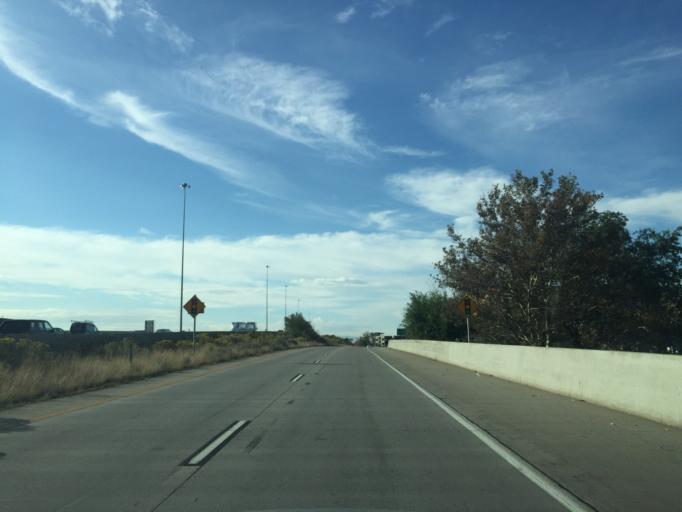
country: US
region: Utah
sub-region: Salt Lake County
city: Murray
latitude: 40.6582
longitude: -111.9018
